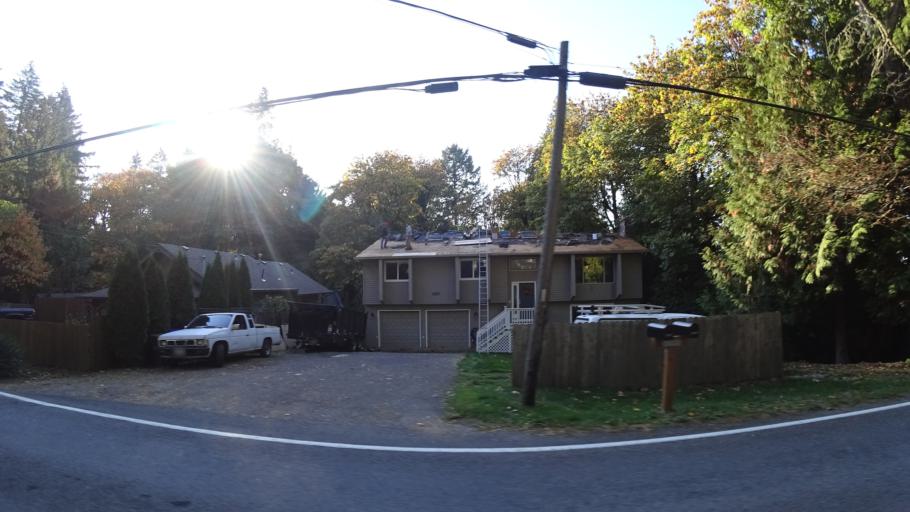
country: US
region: Oregon
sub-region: Multnomah County
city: Gresham
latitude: 45.4737
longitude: -122.4483
